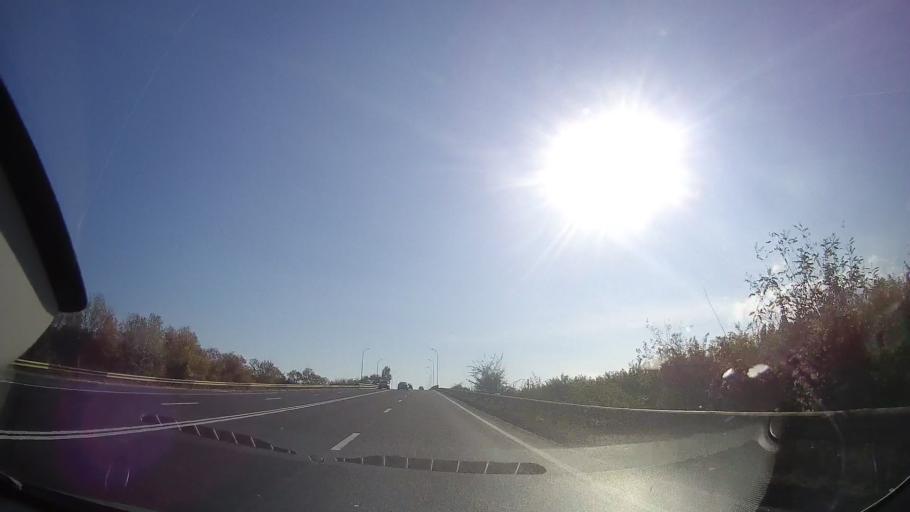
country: RO
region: Constanta
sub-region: Comuna Douazeci si Trei August
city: Dulcesti
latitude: 43.8604
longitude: 28.5755
